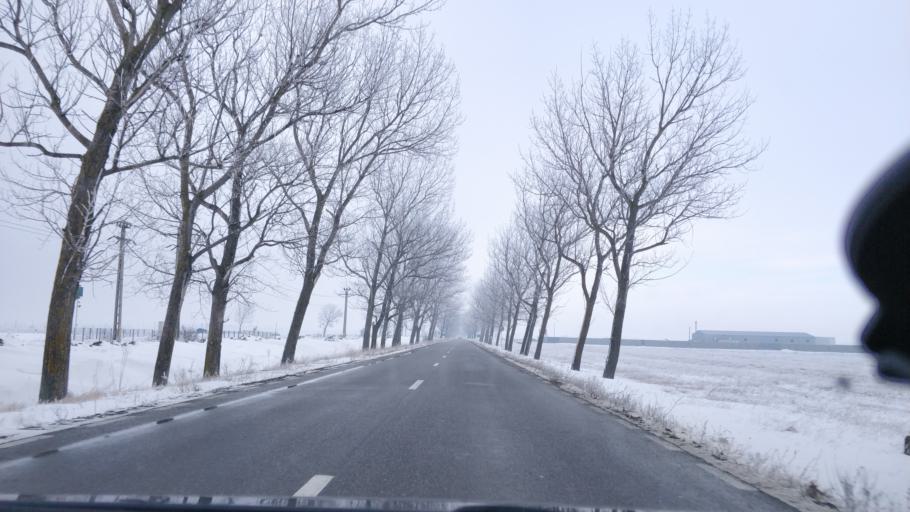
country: RO
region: Vrancea
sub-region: Comuna Vanatori
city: Jorasti
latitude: 45.6974
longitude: 27.2572
